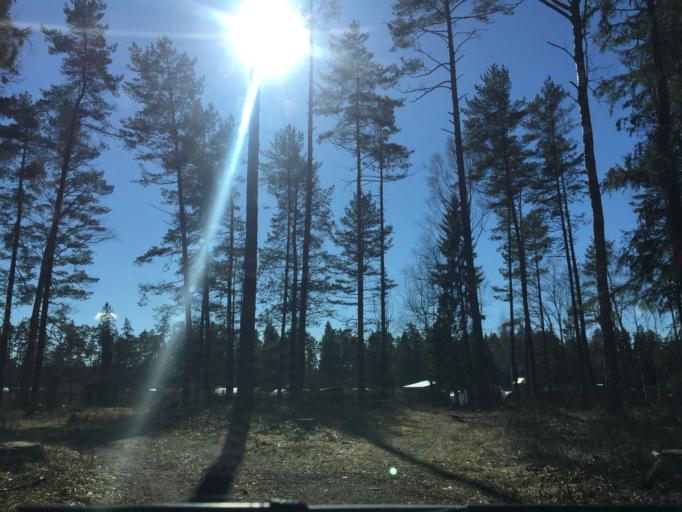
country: LV
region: Incukalns
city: Vangazi
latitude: 57.0911
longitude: 24.5370
